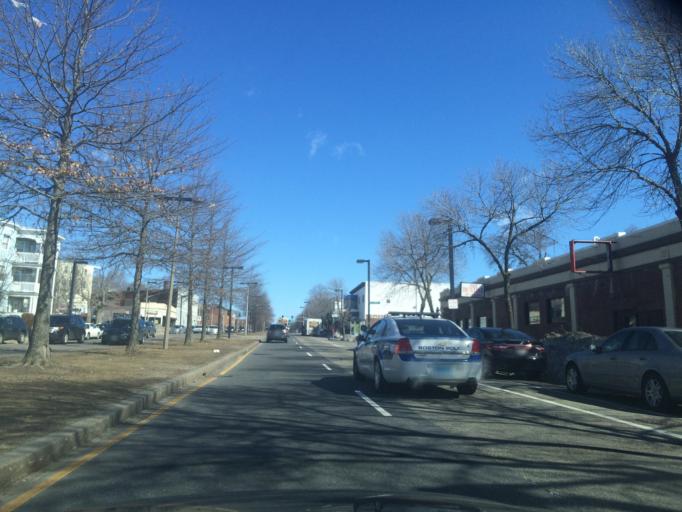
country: US
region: Massachusetts
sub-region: Suffolk County
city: Jamaica Plain
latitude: 42.2888
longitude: -71.0899
